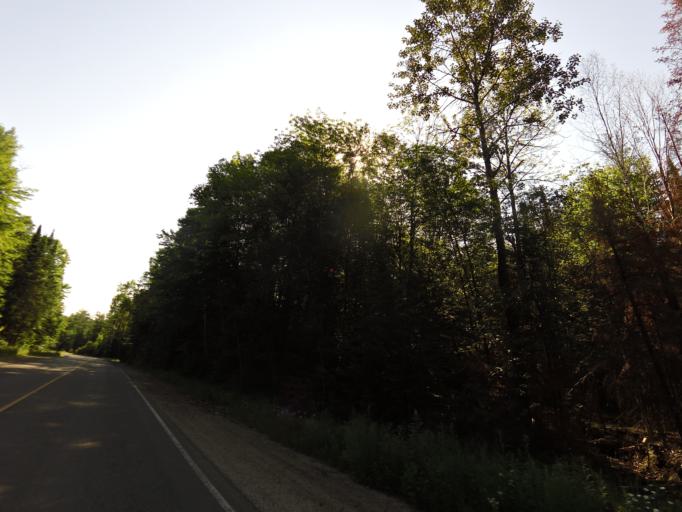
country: CA
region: Ontario
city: Deep River
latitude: 46.1797
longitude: -77.6832
